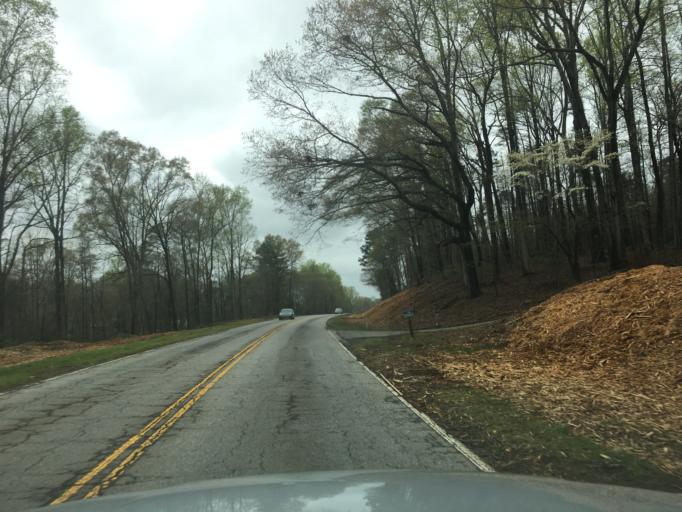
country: US
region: South Carolina
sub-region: Spartanburg County
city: Wellford
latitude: 34.9621
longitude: -82.0833
